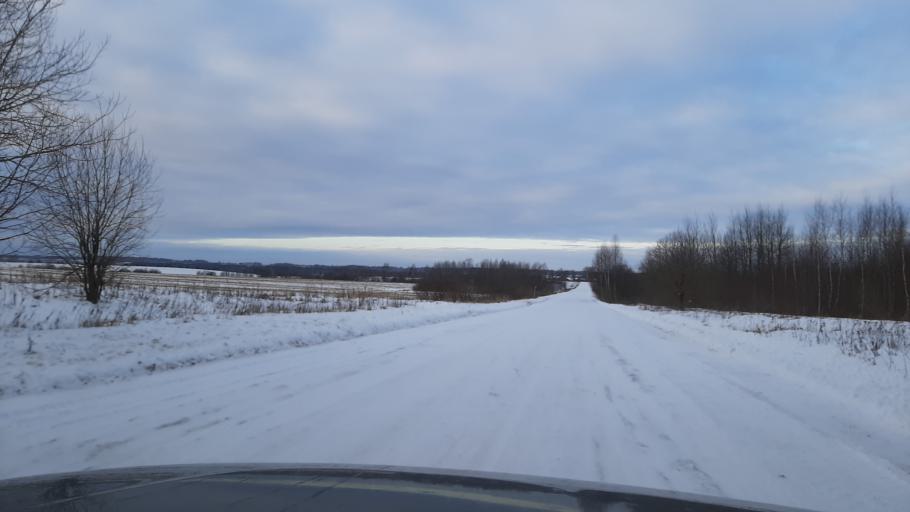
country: RU
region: Kostroma
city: Kosmynino
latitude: 57.4840
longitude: 40.8275
